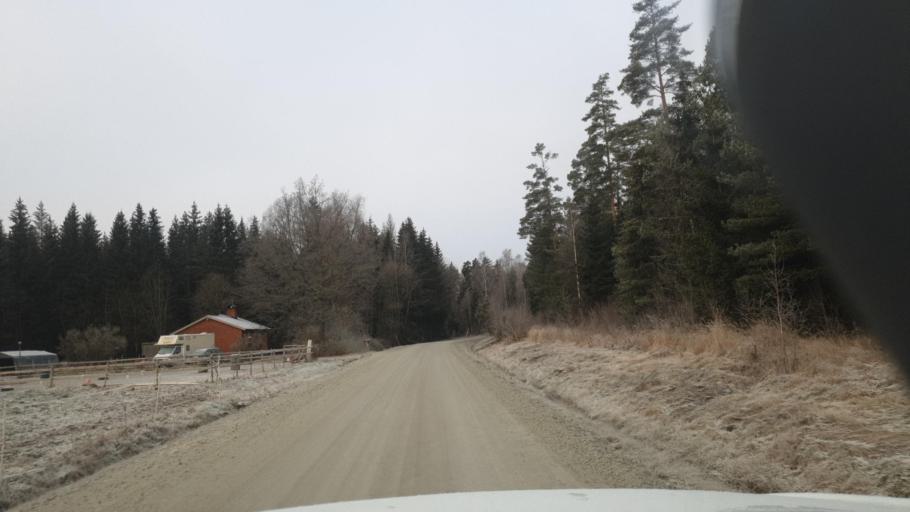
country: SE
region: Vaermland
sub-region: Karlstads Kommun
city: Edsvalla
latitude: 59.4504
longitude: 13.1506
